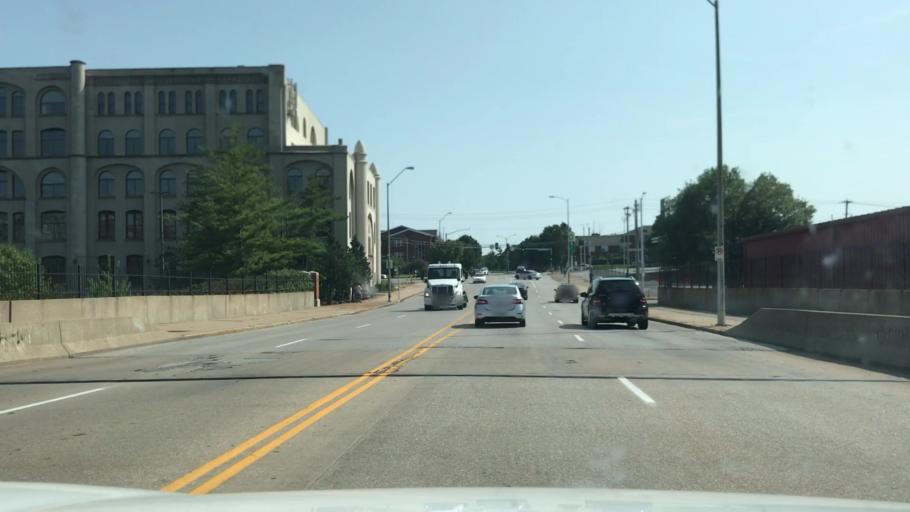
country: US
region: Missouri
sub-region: City of Saint Louis
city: St. Louis
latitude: 38.6209
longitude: -90.2039
